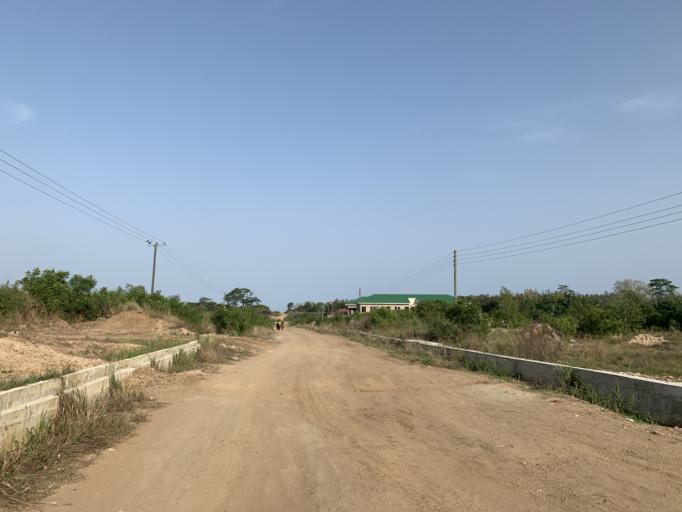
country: GH
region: Central
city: Winneba
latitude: 5.3808
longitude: -0.6206
